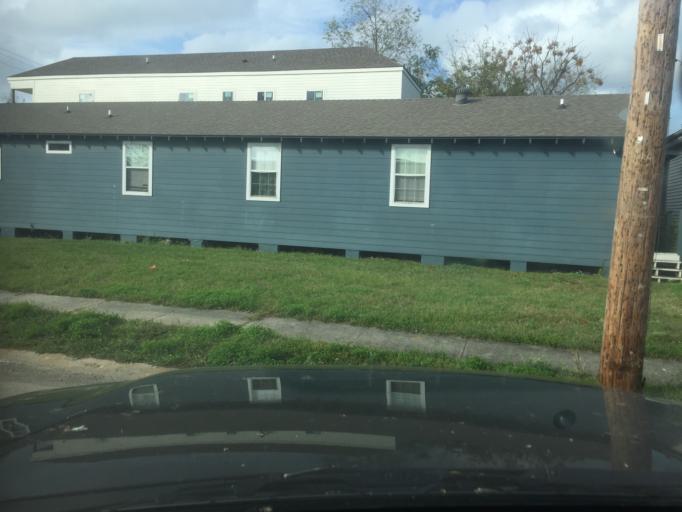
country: US
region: Louisiana
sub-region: Orleans Parish
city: New Orleans
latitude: 29.9929
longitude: -90.0741
